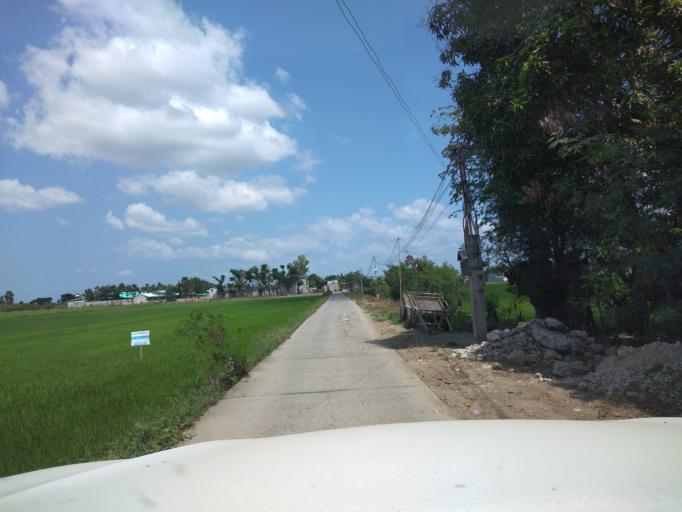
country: PH
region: Central Luzon
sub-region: Province of Pampanga
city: Bahay Pare
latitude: 15.0451
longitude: 120.8787
